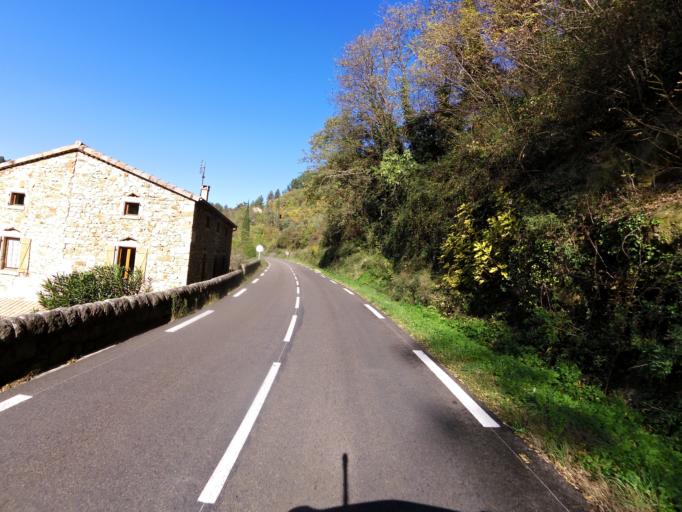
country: FR
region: Rhone-Alpes
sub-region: Departement de l'Ardeche
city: Largentiere
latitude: 44.5314
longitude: 4.2974
